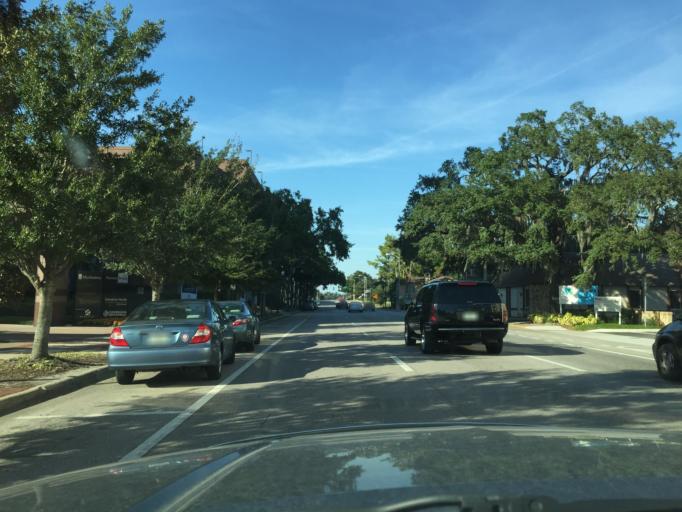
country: US
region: Florida
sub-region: Orange County
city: Orlando
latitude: 28.5552
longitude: -81.3769
